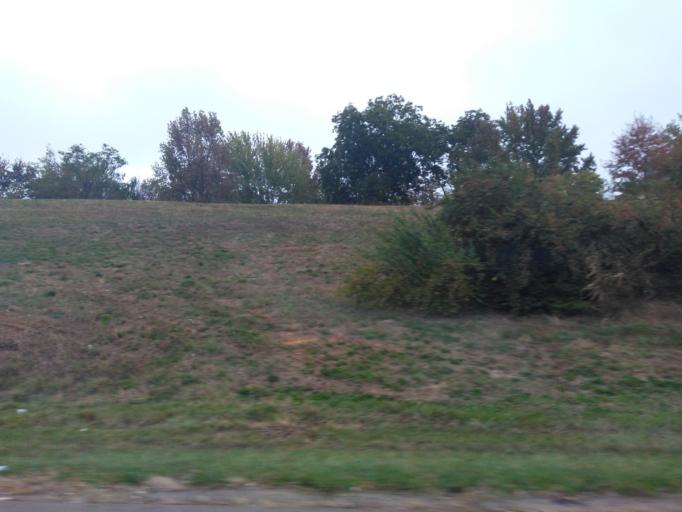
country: US
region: Missouri
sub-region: Saint Louis County
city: Concord
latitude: 38.5097
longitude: -90.3584
